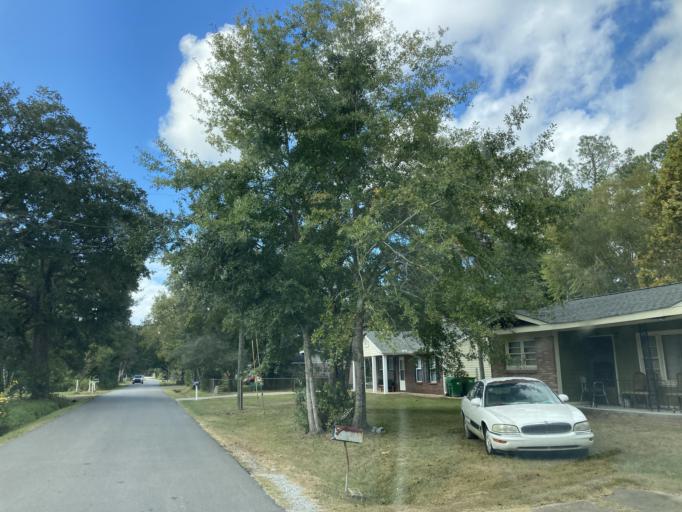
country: US
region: Mississippi
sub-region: Jackson County
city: Gulf Hills
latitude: 30.4431
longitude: -88.8320
